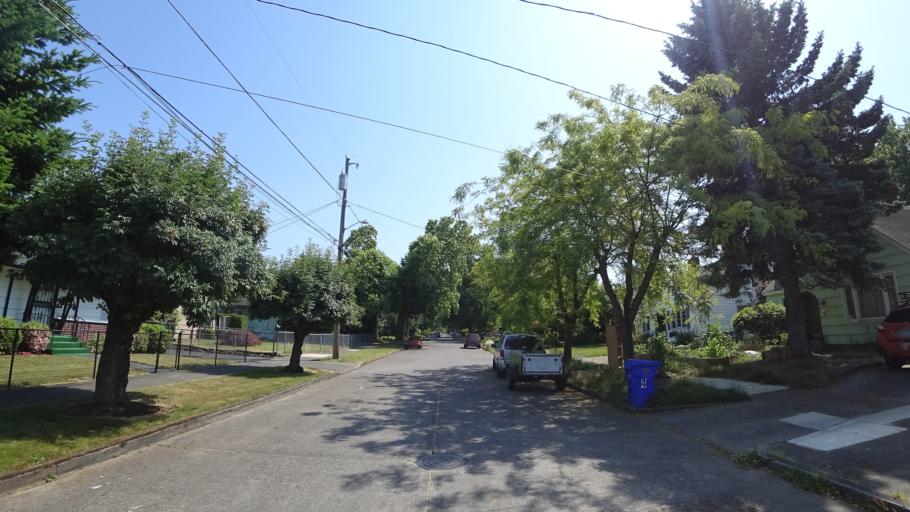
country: US
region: Oregon
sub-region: Multnomah County
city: Portland
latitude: 45.5797
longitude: -122.7068
